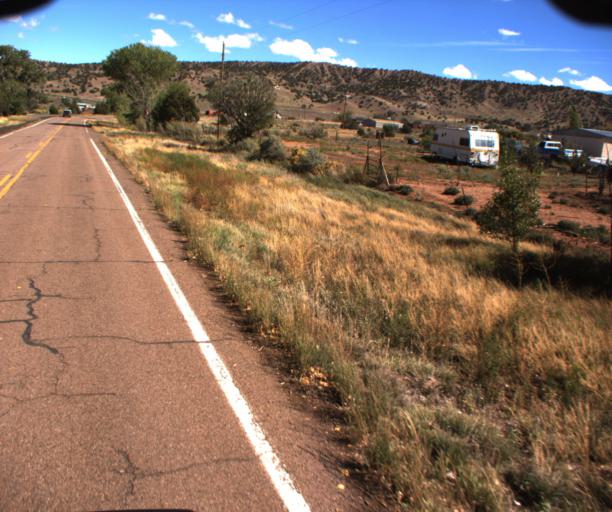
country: US
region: Arizona
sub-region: Apache County
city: Saint Johns
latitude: 34.4781
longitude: -109.6068
